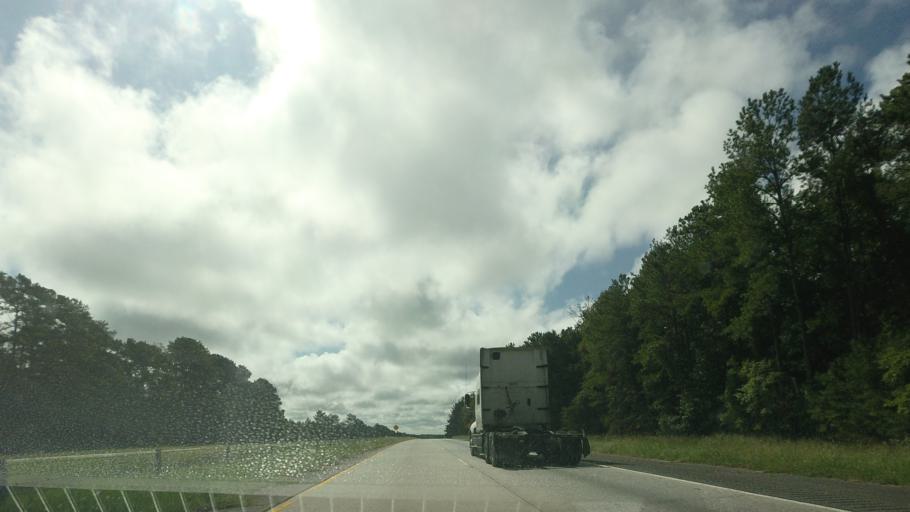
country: US
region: Georgia
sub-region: Houston County
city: Robins Air Force Base
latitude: 32.6849
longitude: -83.4895
